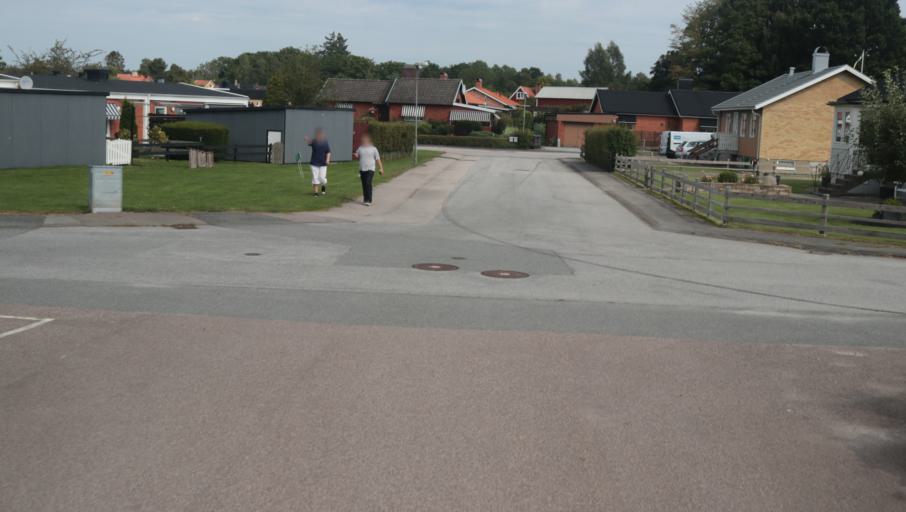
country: SE
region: Blekinge
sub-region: Karlshamns Kommun
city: Morrum
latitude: 56.1997
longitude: 14.7385
